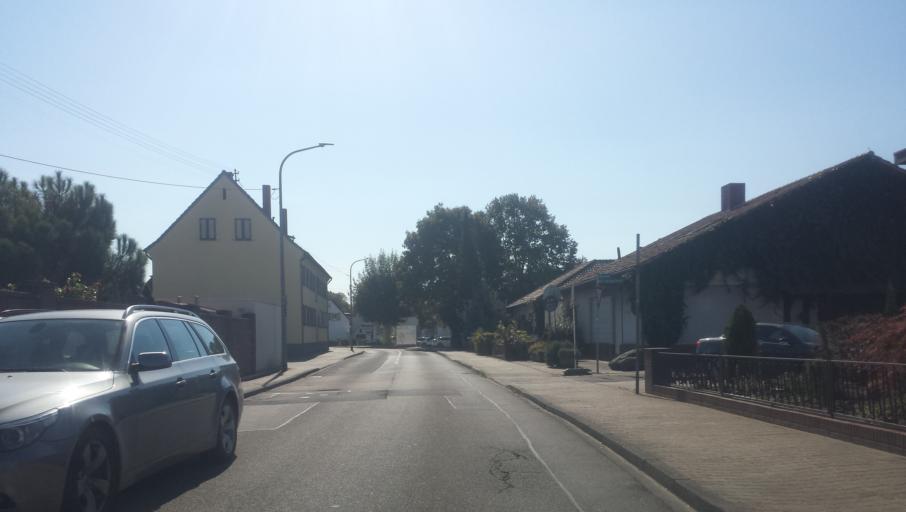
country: DE
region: Rheinland-Pfalz
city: Neuhofen
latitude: 49.4243
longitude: 8.4226
